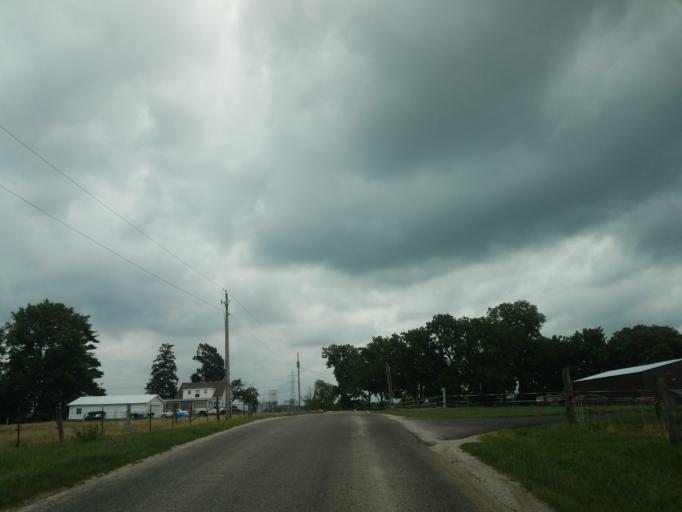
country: US
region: Illinois
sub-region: McLean County
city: Bloomington
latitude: 40.4746
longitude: -89.0346
